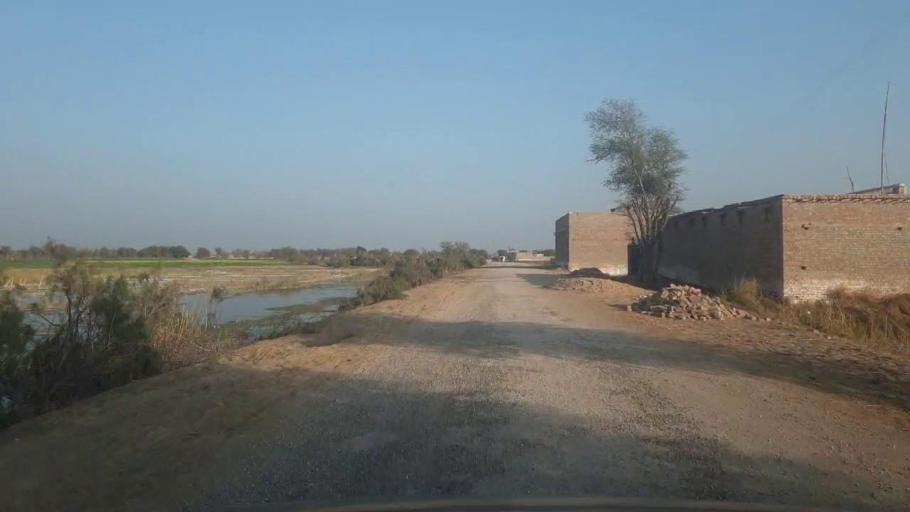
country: PK
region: Sindh
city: Sakrand
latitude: 26.0560
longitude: 68.3880
